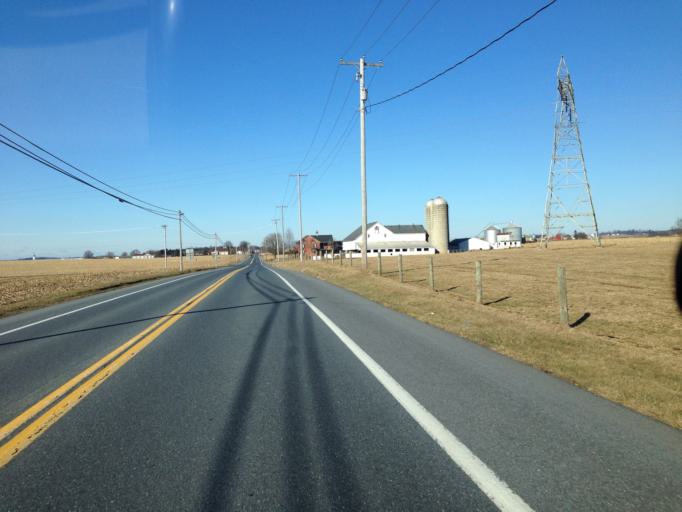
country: US
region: Pennsylvania
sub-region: Lancaster County
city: Lititz
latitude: 40.1709
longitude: -76.3275
